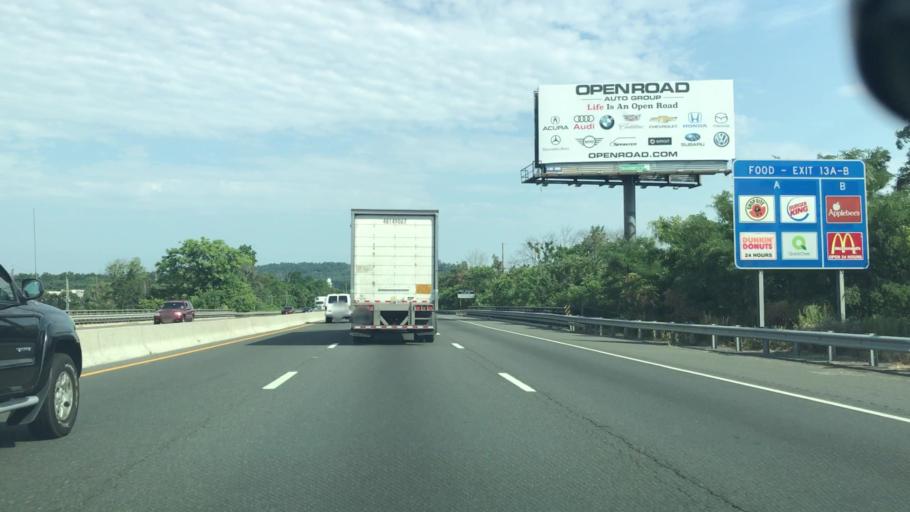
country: US
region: New Jersey
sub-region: Somerset County
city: Bound Brook
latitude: 40.5596
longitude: -74.5484
